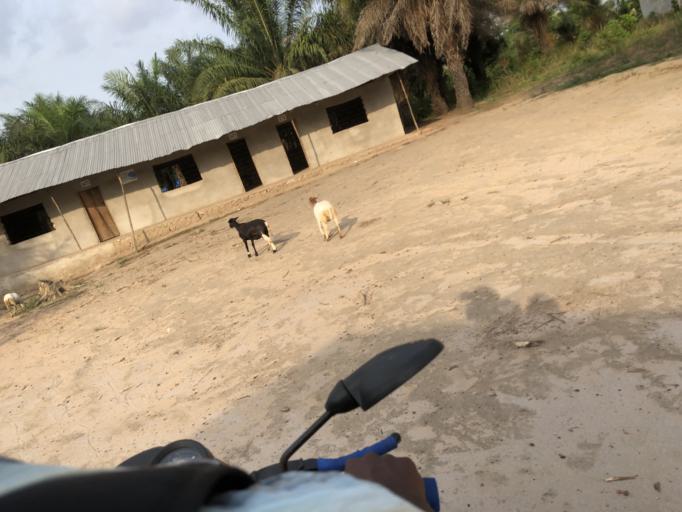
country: SL
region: Northern Province
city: Yonibana
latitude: 8.4635
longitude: -12.2033
